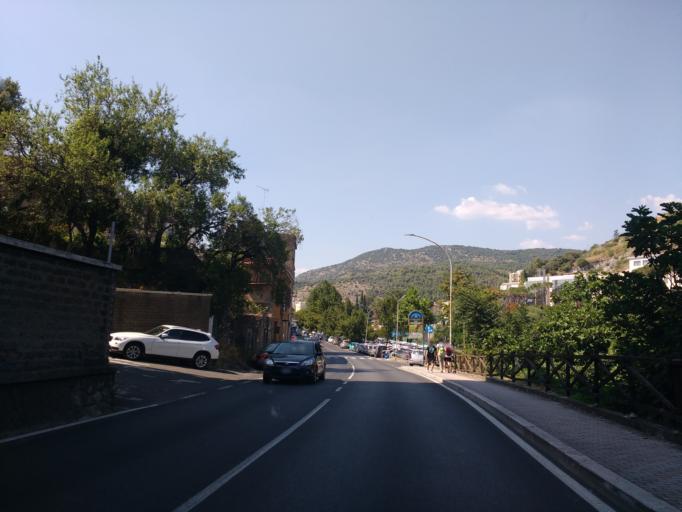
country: IT
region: Latium
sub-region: Citta metropolitana di Roma Capitale
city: Tivoli
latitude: 41.9612
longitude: 12.8030
